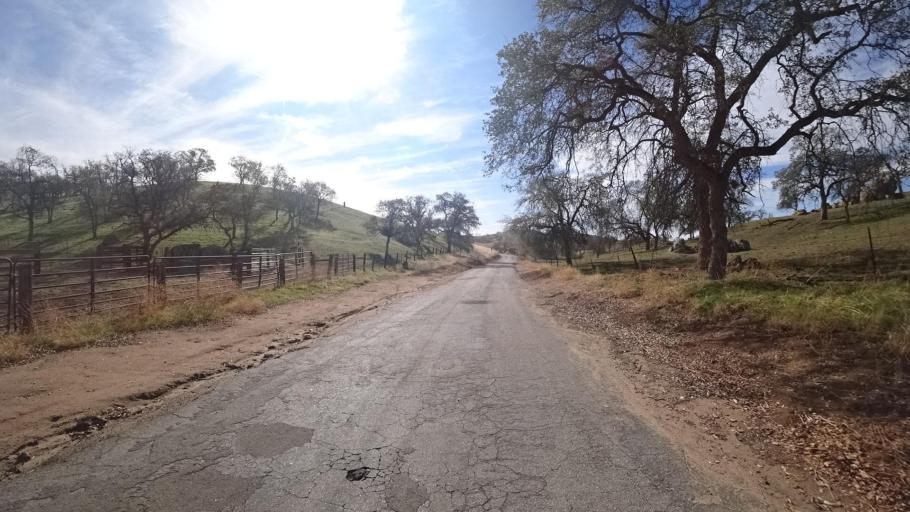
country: US
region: California
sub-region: Kern County
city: Oildale
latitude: 35.6177
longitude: -118.8471
